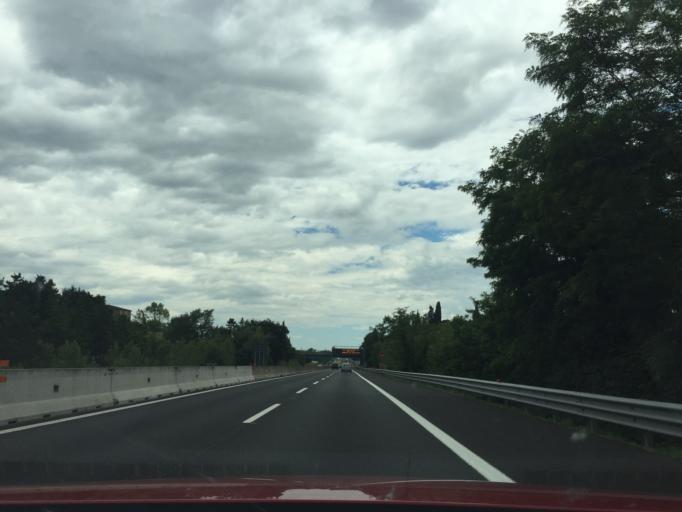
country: IT
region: Tuscany
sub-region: Provincia di Pistoia
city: Pieve a Nievole
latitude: 43.8872
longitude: 10.8201
